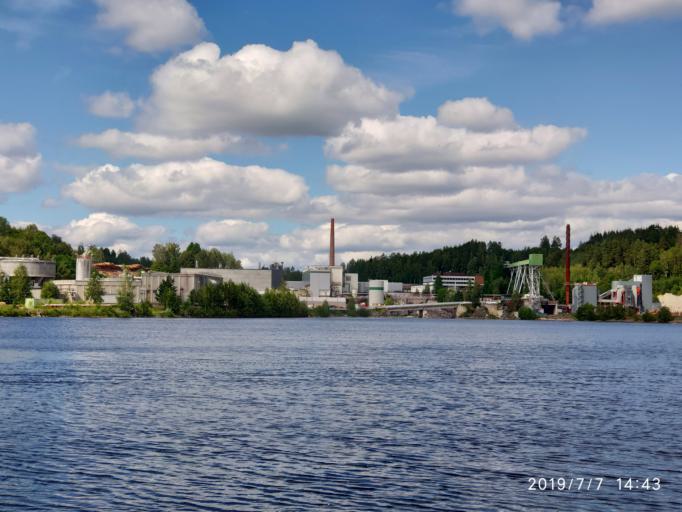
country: NO
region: Buskerud
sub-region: Ringerike
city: Honefoss
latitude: 60.1777
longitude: 10.2439
